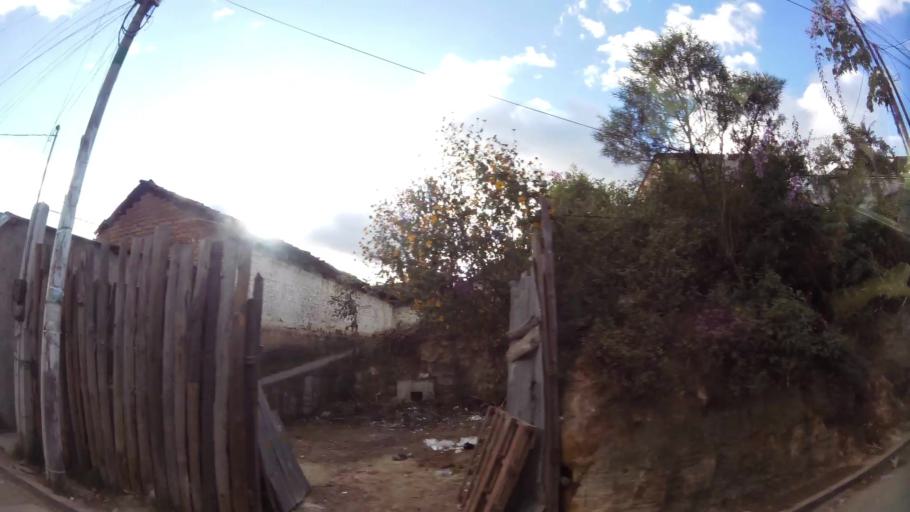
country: GT
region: Quiche
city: Chichicastenango
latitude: 14.9457
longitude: -91.1113
